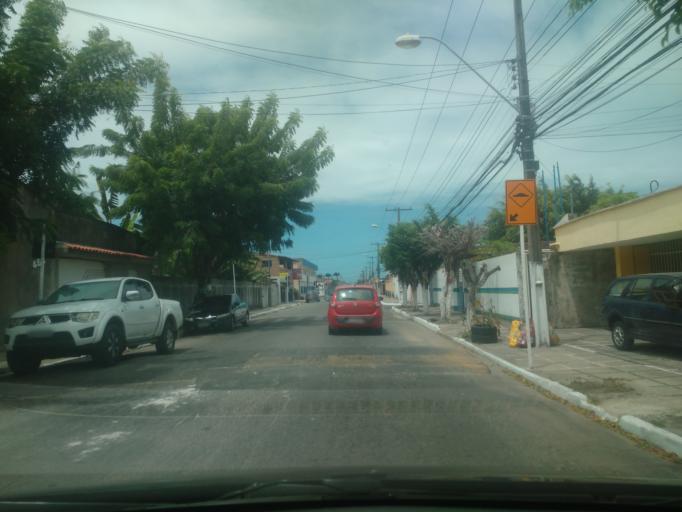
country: BR
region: Alagoas
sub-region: Satuba
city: Satuba
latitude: -9.5529
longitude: -35.7634
